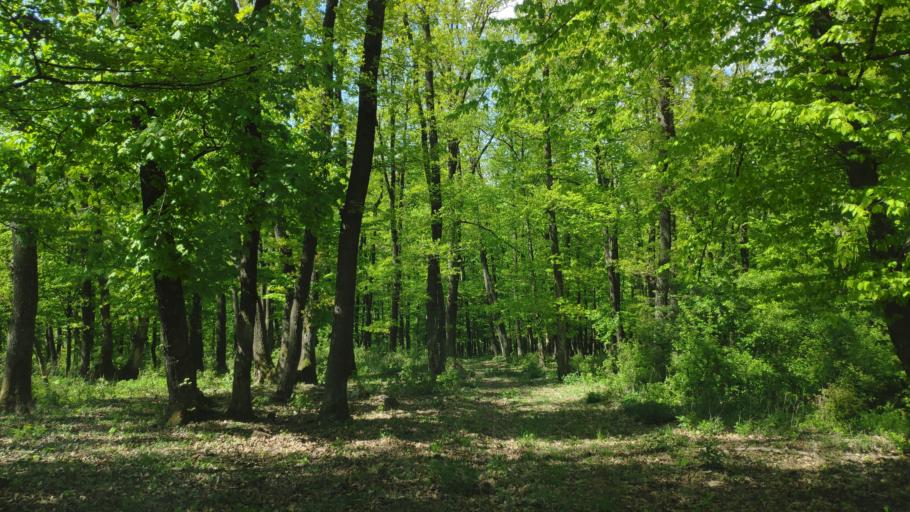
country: SK
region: Kosicky
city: Kosice
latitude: 48.6660
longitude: 21.4405
